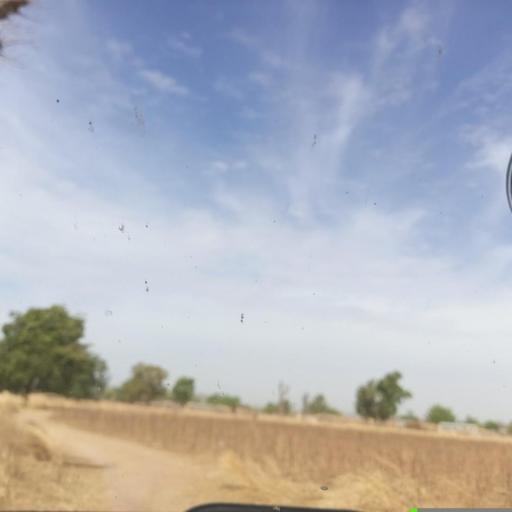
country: ML
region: Koulikoro
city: Koulikoro
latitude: 13.1255
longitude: -7.7069
